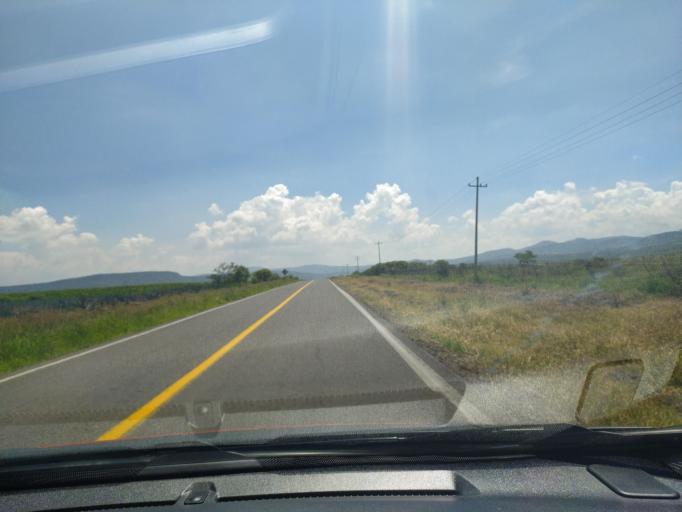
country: MX
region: Guanajuato
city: Ciudad Manuel Doblado
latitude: 20.6758
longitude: -101.9404
